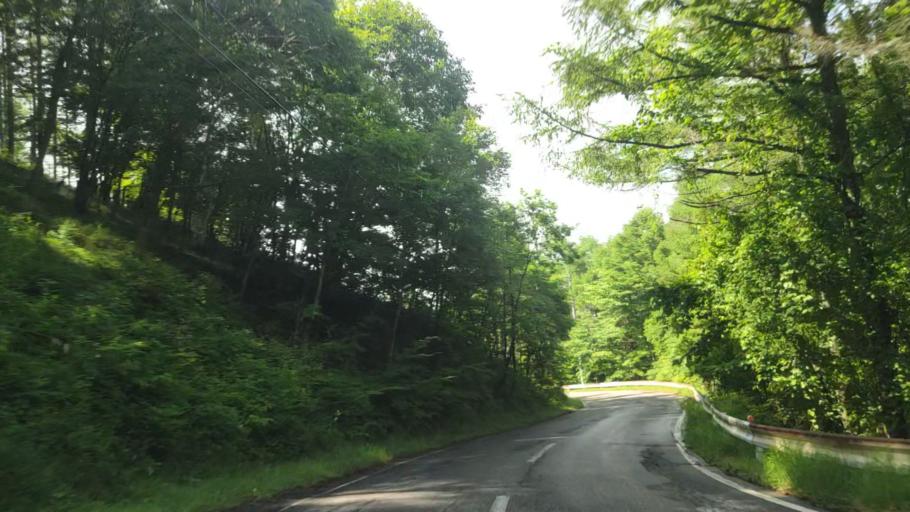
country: JP
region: Nagano
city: Suwa
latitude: 36.0923
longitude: 138.1455
